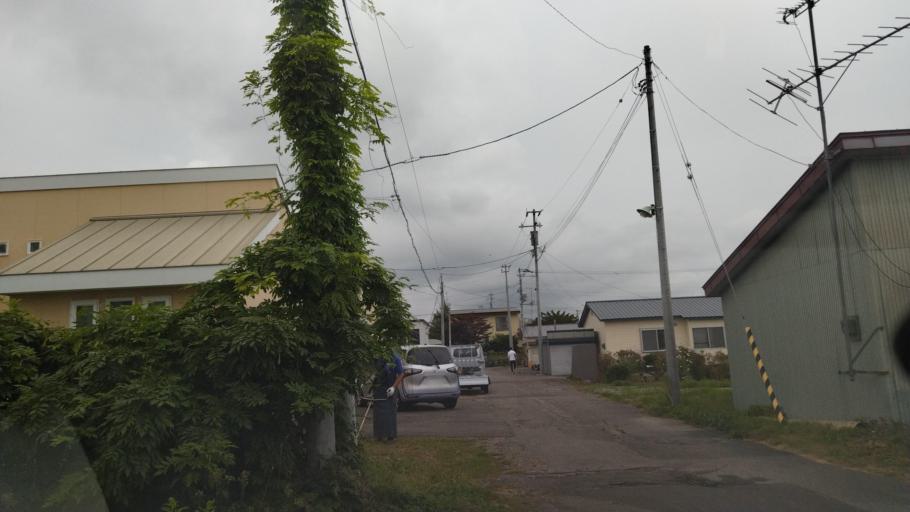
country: JP
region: Hokkaido
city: Otofuke
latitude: 43.2304
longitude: 143.2935
